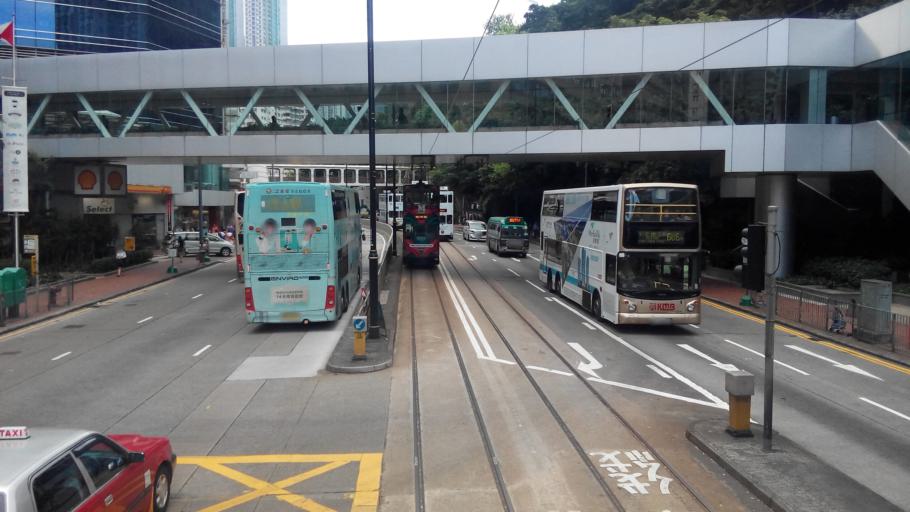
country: HK
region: Wanchai
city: Wan Chai
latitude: 22.2875
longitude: 114.2101
